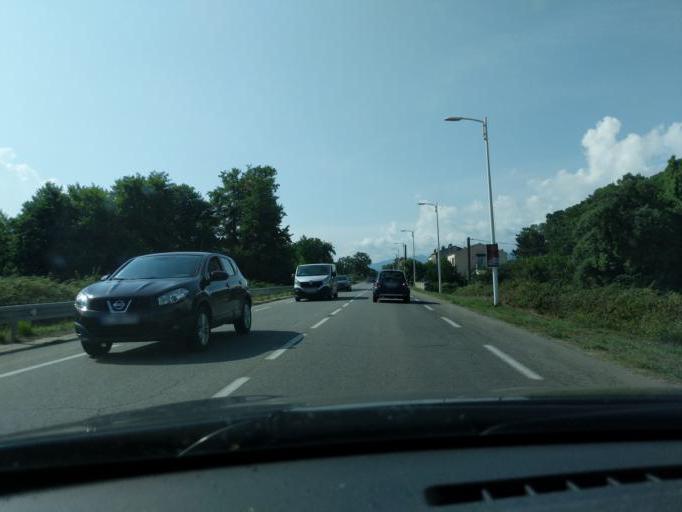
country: FR
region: Corsica
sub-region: Departement de la Haute-Corse
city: Ghisonaccia
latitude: 41.9543
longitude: 9.3958
